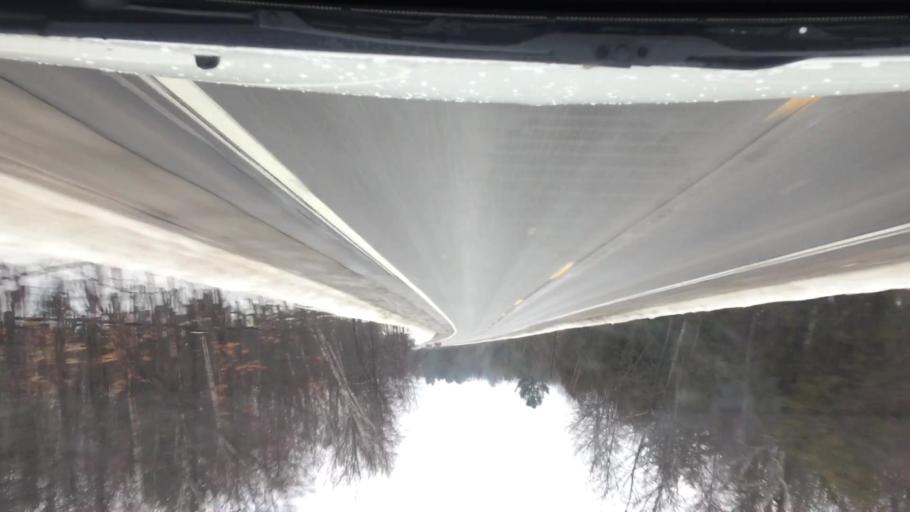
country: US
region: Michigan
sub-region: Charlevoix County
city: Charlevoix
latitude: 45.2625
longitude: -85.1951
